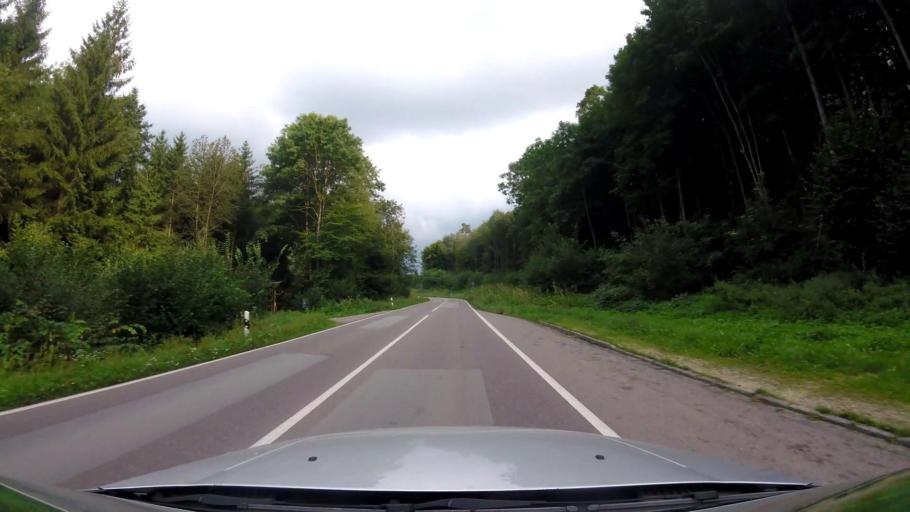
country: DE
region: Baden-Wuerttemberg
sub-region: Regierungsbezirk Stuttgart
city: Durlangen
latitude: 48.8424
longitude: 9.7841
